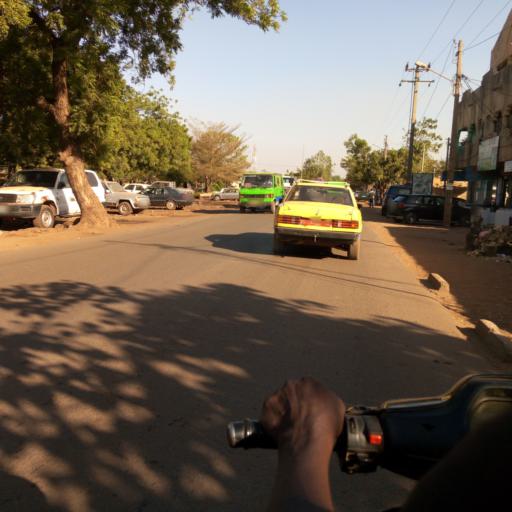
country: ML
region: Bamako
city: Bamako
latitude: 12.6557
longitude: -8.0251
